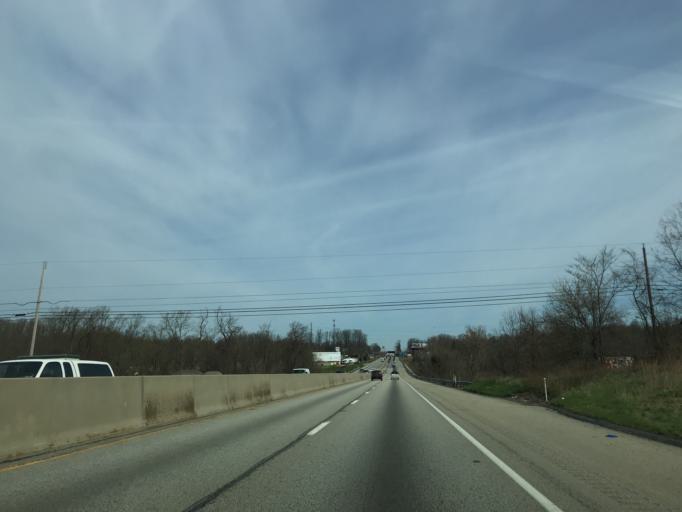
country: US
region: Pennsylvania
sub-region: York County
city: Valley Green
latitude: 40.1194
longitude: -76.7882
